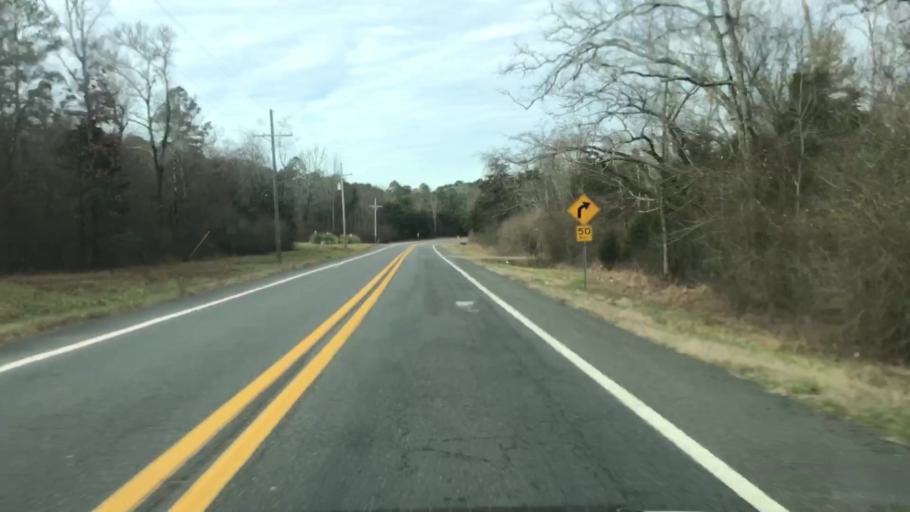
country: US
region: Arkansas
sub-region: Montgomery County
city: Mount Ida
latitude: 34.6084
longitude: -93.6808
